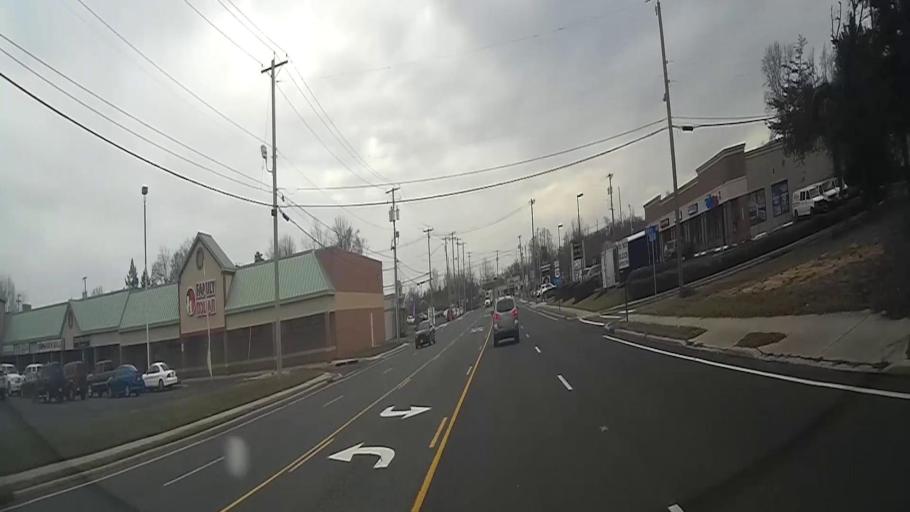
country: US
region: New Jersey
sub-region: Camden County
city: Berlin
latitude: 39.8001
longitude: -74.9323
